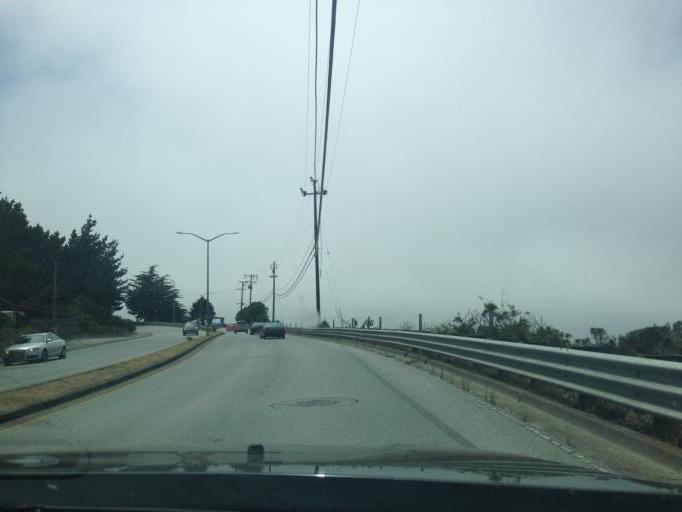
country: US
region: California
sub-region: San Mateo County
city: Pacifica
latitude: 37.6339
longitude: -122.4753
